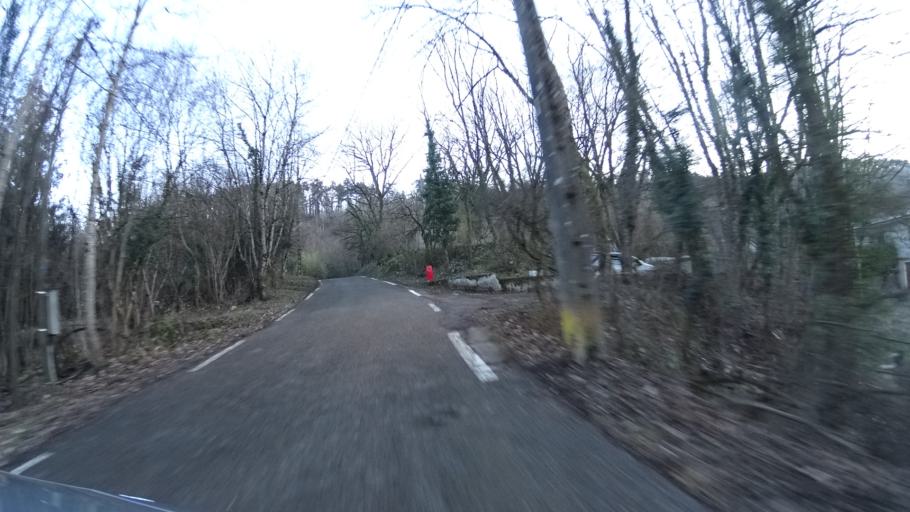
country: FR
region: Franche-Comte
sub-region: Departement du Doubs
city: Morre
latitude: 47.2197
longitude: 6.0415
